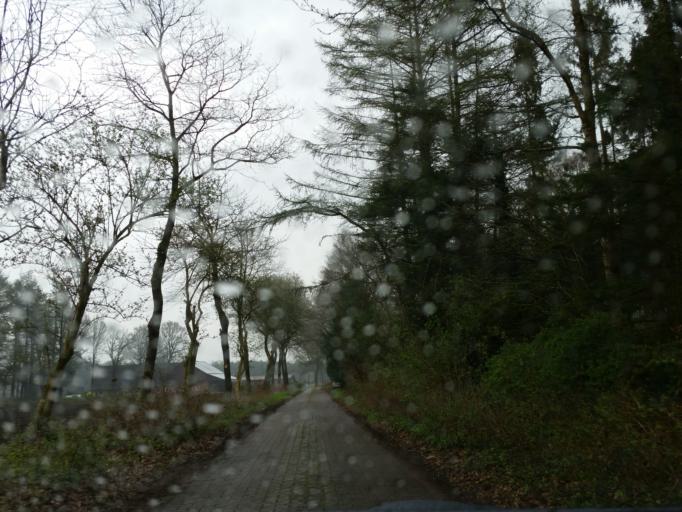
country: DE
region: Lower Saxony
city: Hipstedt
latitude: 53.5667
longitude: 8.9764
